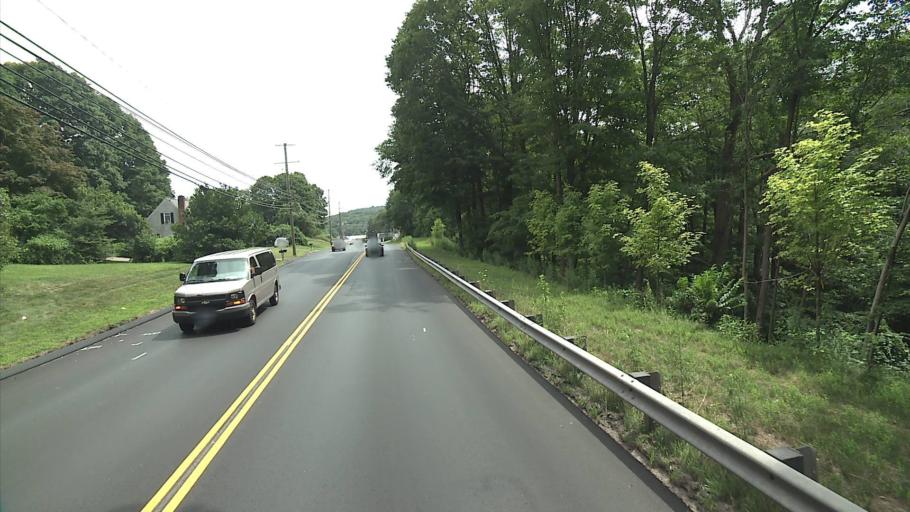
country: US
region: Connecticut
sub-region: New Haven County
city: Seymour
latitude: 41.4126
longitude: -73.0986
